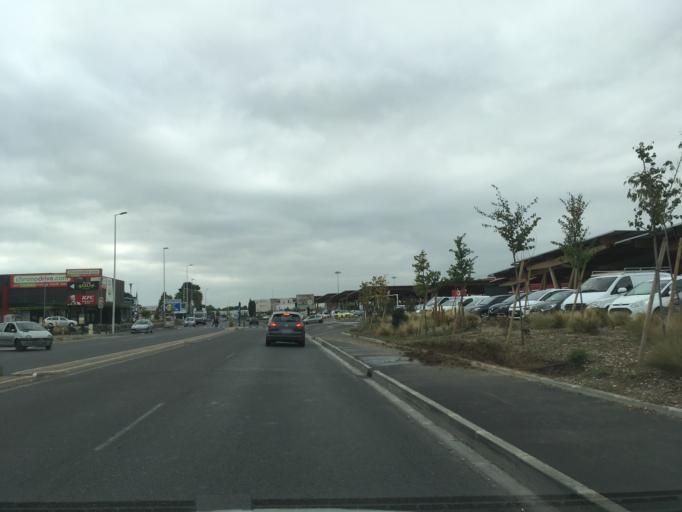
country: FR
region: Languedoc-Roussillon
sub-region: Departement de l'Herault
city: Lattes
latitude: 43.5876
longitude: 3.8898
